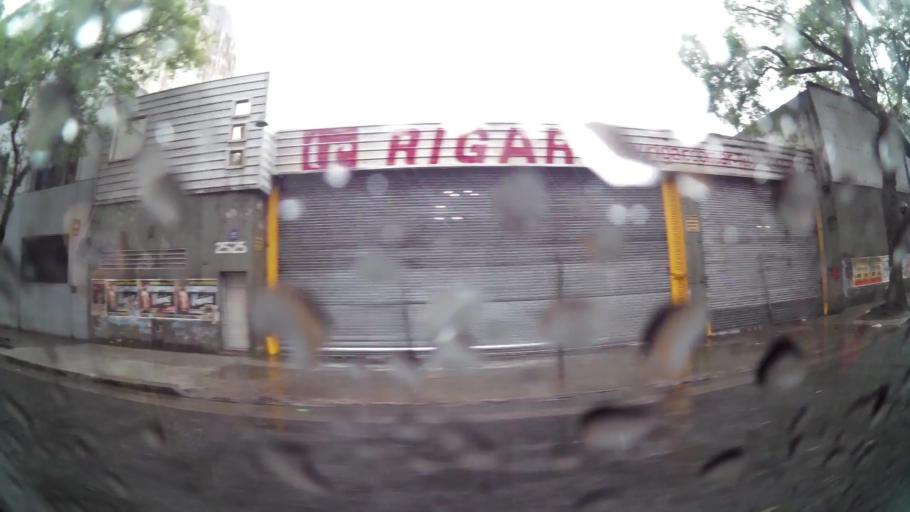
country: AR
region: Buenos Aires
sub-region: Partido de Avellaneda
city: Avellaneda
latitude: -34.6427
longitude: -58.3967
